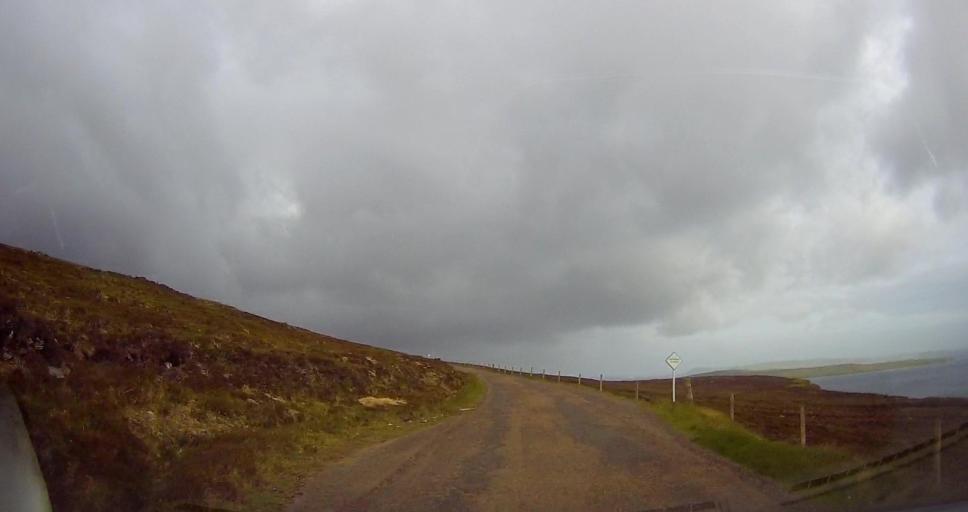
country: GB
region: Scotland
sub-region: Orkney Islands
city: Stromness
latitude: 58.8928
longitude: -3.2631
